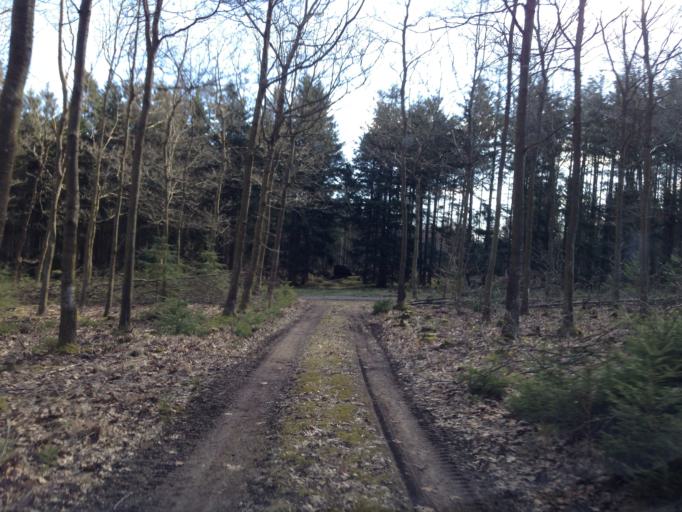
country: DK
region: Central Jutland
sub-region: Holstebro Kommune
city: Ulfborg
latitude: 56.2611
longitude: 8.4731
